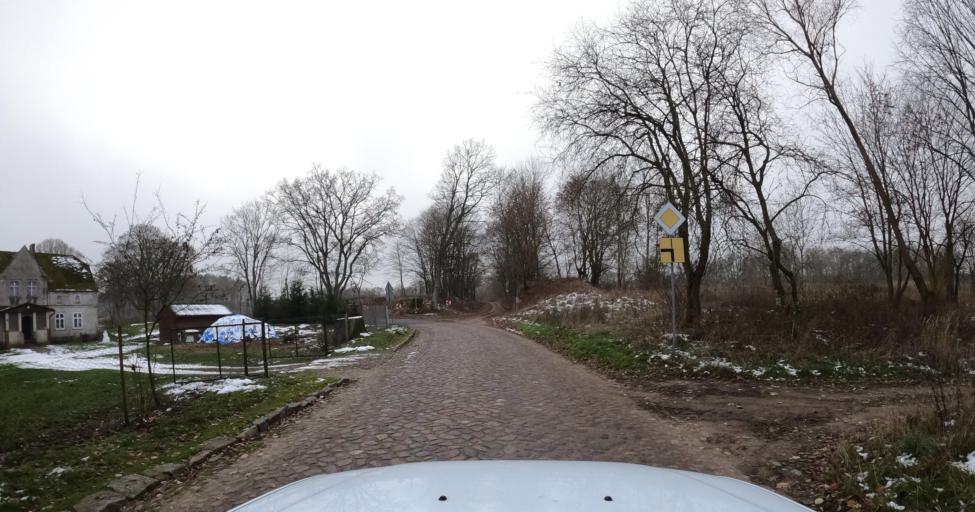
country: PL
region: West Pomeranian Voivodeship
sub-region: Powiat swidwinski
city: Swidwin
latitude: 53.8704
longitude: 15.8301
